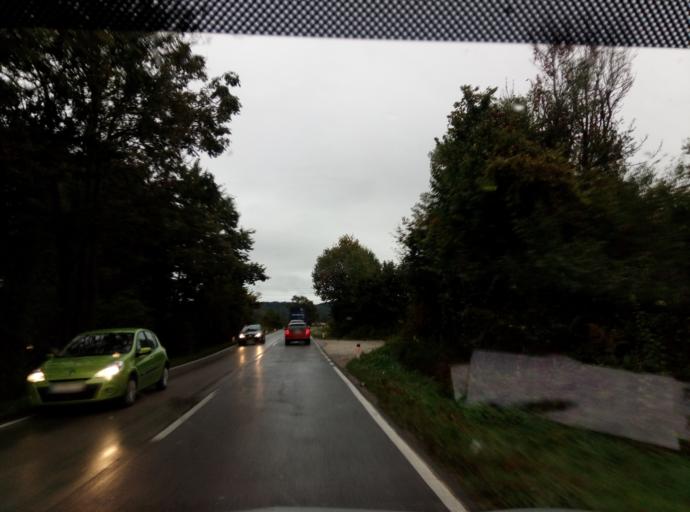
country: SI
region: Ljubljana
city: Ljubljana
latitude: 46.1045
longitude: 14.4808
